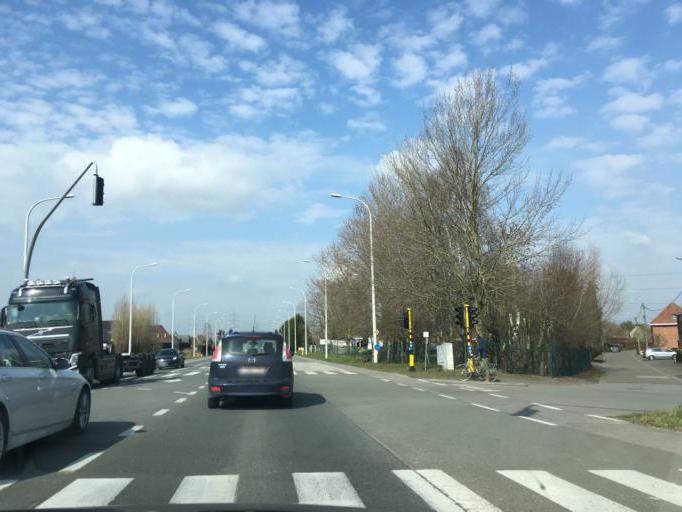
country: BE
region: Flanders
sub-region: Provincie West-Vlaanderen
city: Lendelede
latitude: 50.8898
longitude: 3.2482
